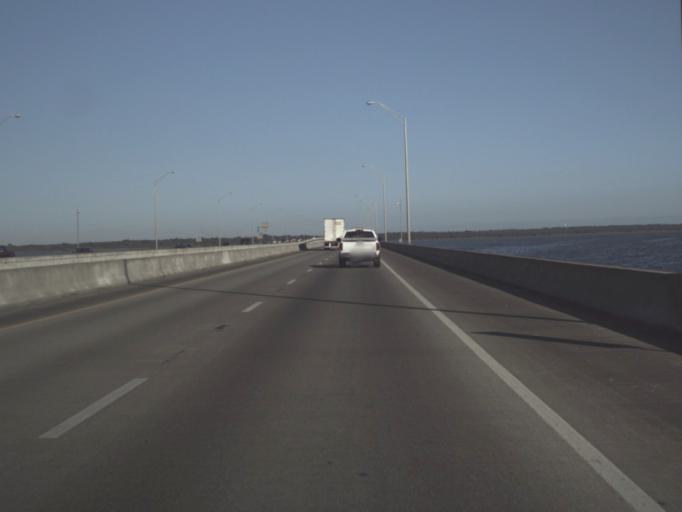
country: US
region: Florida
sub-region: Seminole County
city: Oviedo
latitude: 28.7066
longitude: -81.2359
